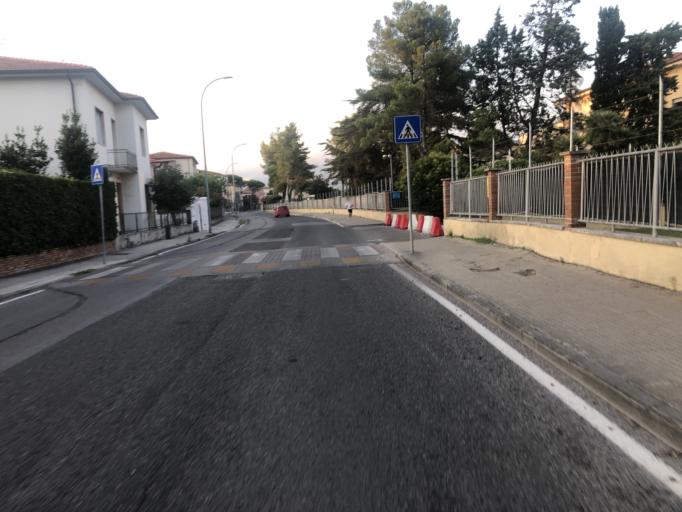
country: IT
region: Tuscany
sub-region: Province of Pisa
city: Pisa
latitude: 43.7298
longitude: 10.4068
